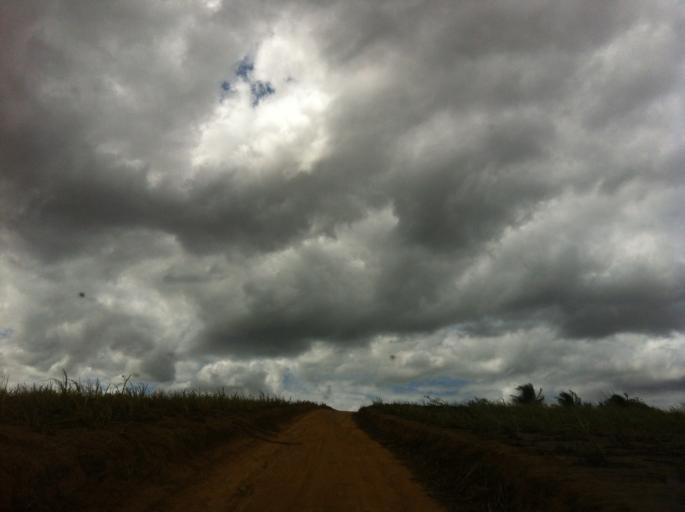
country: BR
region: Alagoas
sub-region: Ibateguara
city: Ibateguara
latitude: -8.9534
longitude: -35.9533
